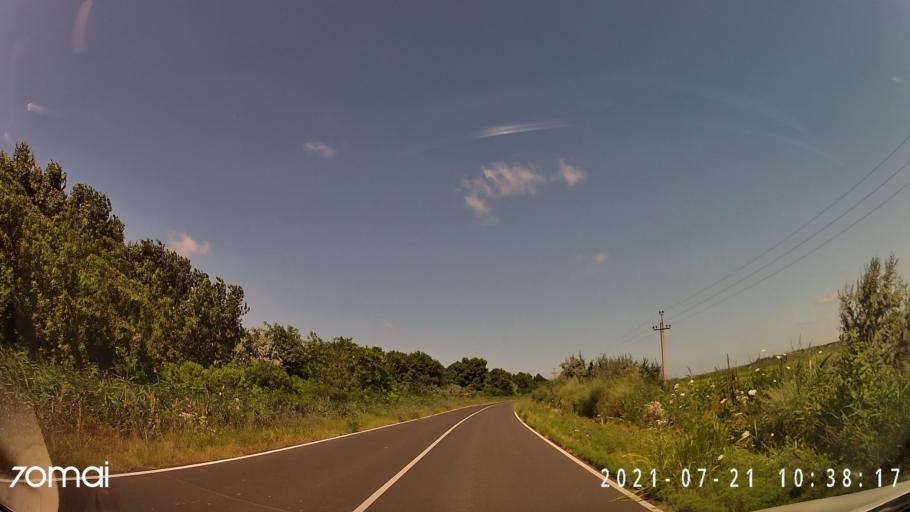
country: RO
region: Tulcea
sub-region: Oras Isaccea
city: Isaccea
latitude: 45.2966
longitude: 28.4415
